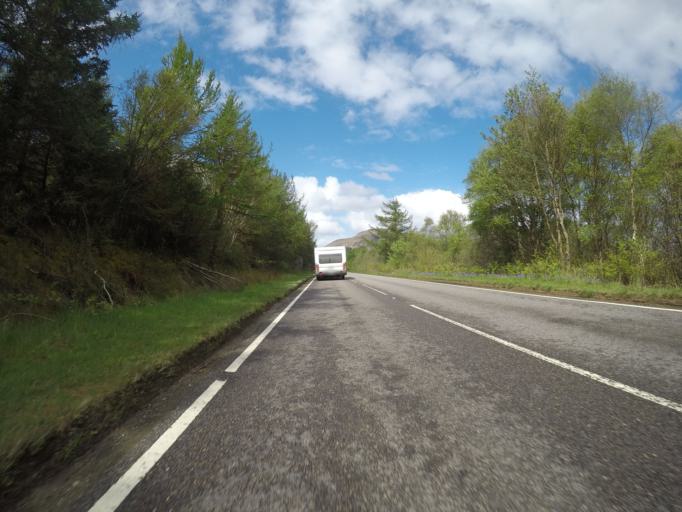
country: GB
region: Scotland
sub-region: Highland
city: Portree
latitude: 57.2599
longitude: -5.9436
